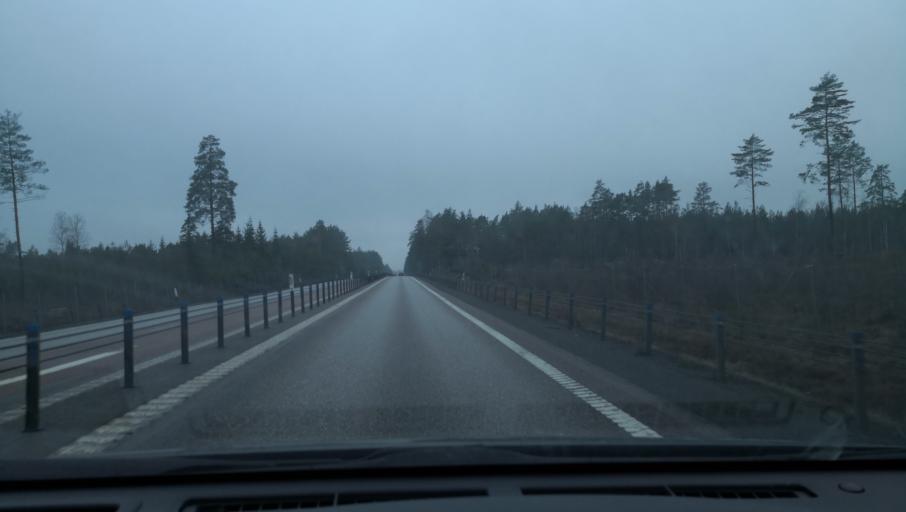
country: SE
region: OErebro
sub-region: Laxa Kommun
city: Laxa
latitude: 58.9931
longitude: 14.6631
